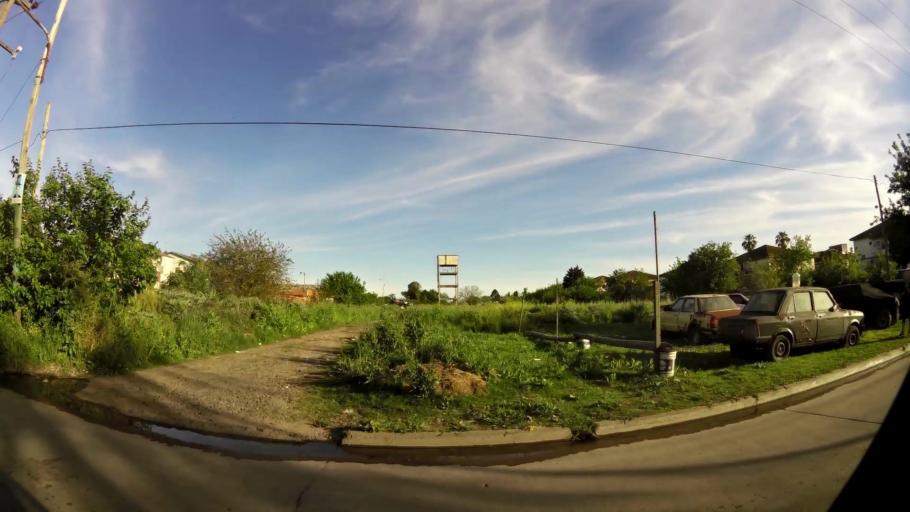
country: AR
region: Buenos Aires
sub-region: Partido de Almirante Brown
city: Adrogue
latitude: -34.8165
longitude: -58.3322
